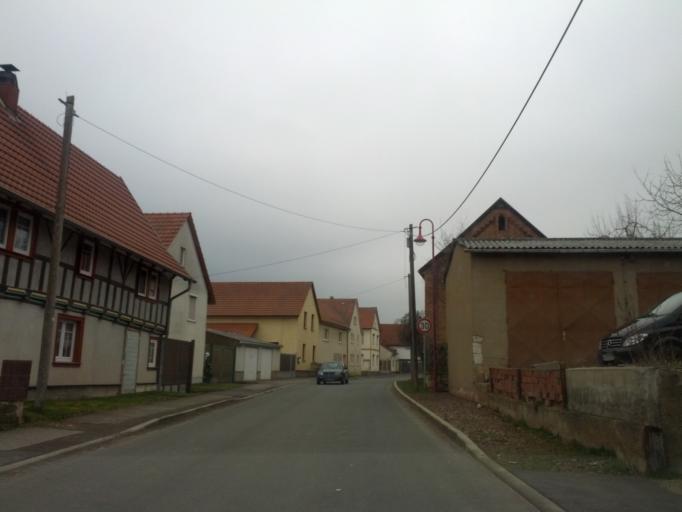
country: DE
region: Thuringia
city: Sonneborn
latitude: 51.0343
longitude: 10.5850
